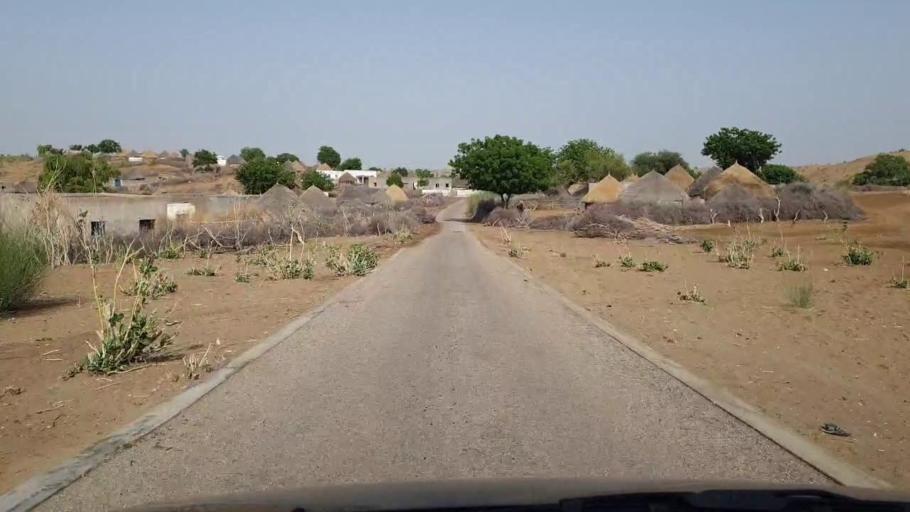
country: PK
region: Sindh
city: Chor
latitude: 25.4542
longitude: 70.5195
